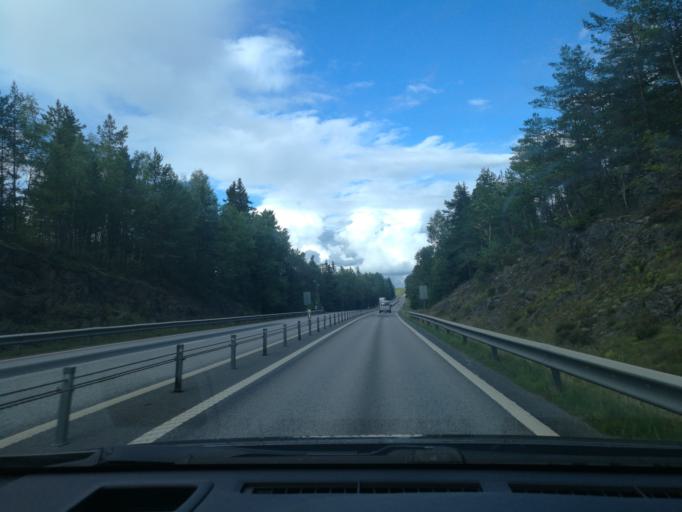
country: SE
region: OEstergoetland
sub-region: Norrkopings Kommun
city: Jursla
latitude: 58.7154
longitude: 16.1641
